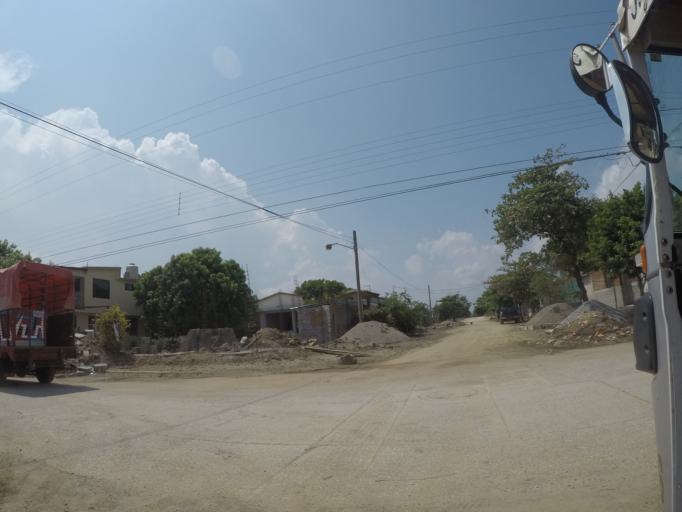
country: MX
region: Oaxaca
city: Union Hidalgo
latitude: 16.4681
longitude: -94.8313
